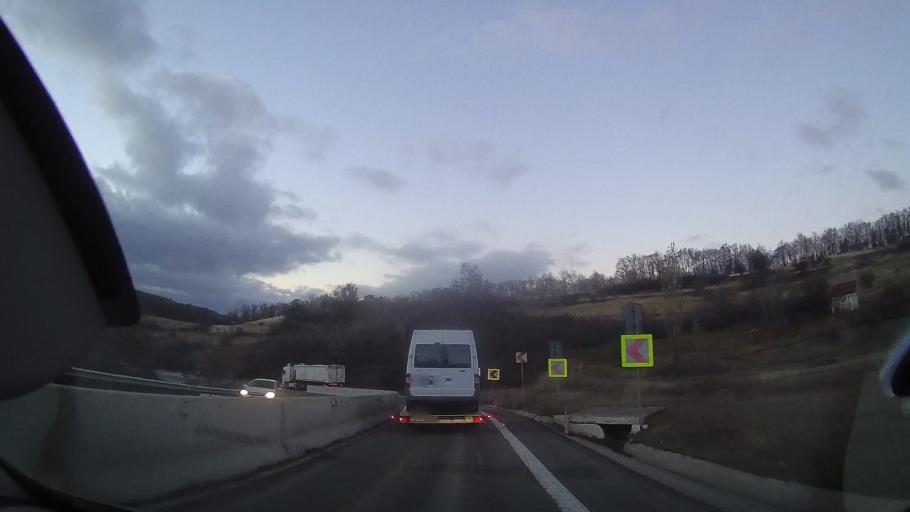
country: RO
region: Cluj
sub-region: Comuna Izvoru Crisului
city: Izvoru Crisului
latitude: 46.8290
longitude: 23.1523
